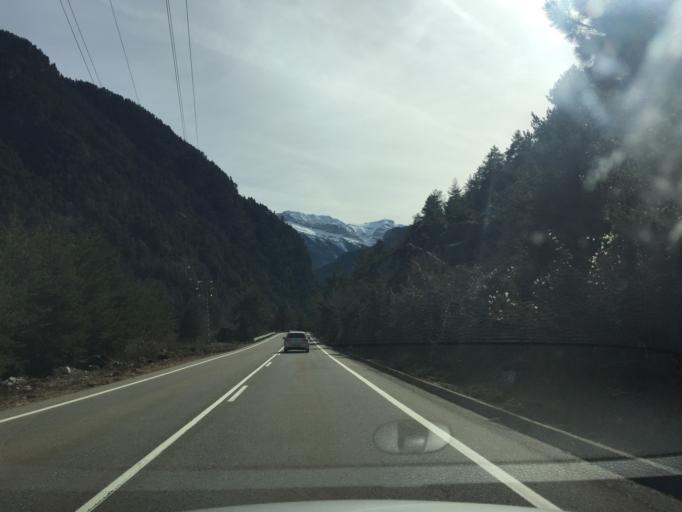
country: ES
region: Aragon
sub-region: Provincia de Huesca
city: Bielsa
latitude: 42.6723
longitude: 0.2146
